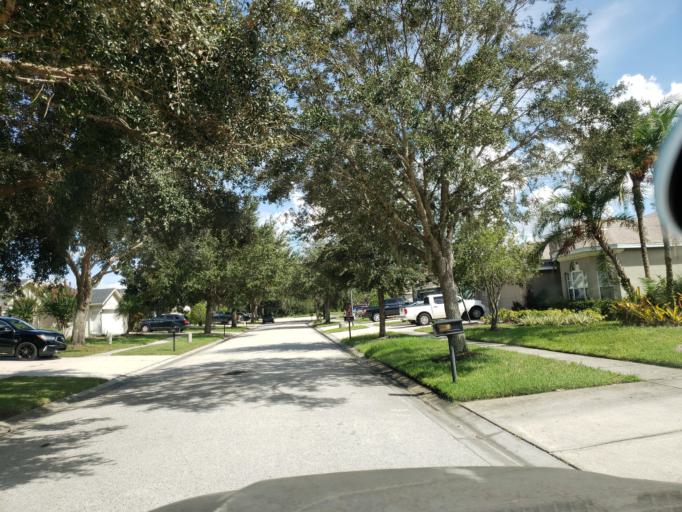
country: US
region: Florida
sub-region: Hillsborough County
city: Fish Hawk
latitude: 27.8334
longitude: -82.2143
